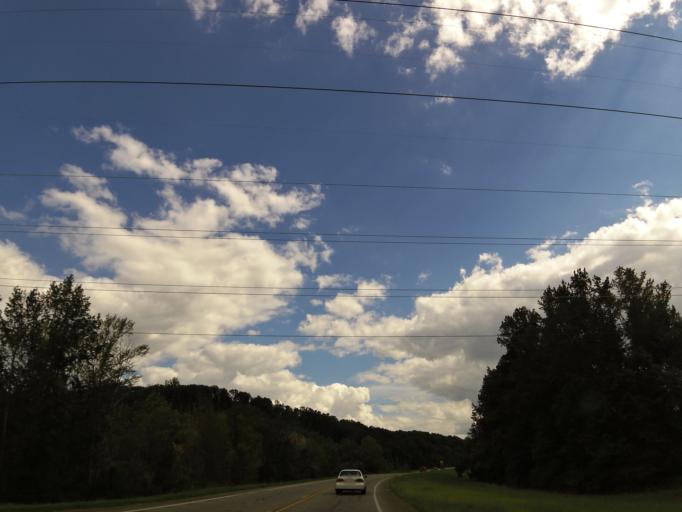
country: US
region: Georgia
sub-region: Walker County
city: Chattanooga Valley
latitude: 34.9546
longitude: -85.3334
